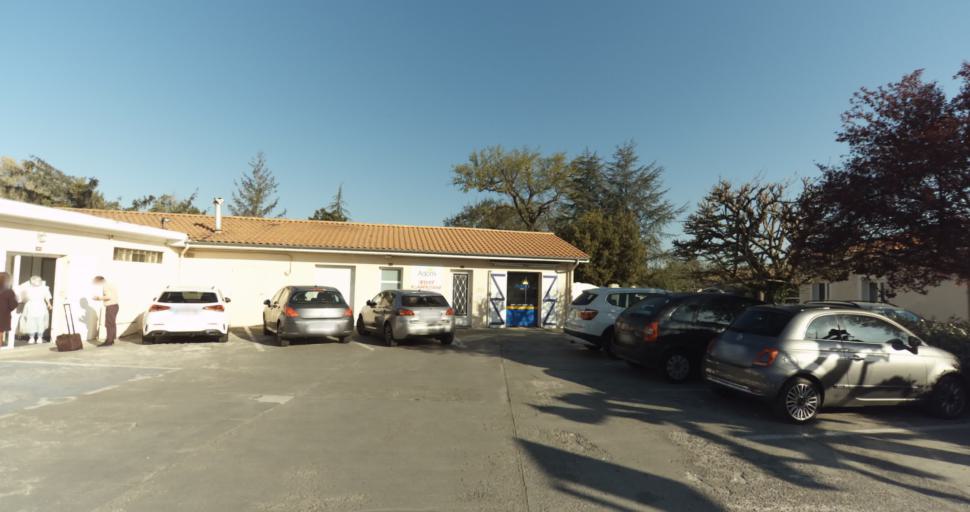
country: FR
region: Aquitaine
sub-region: Departement de la Gironde
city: Martignas-sur-Jalle
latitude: 44.8091
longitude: -0.7852
